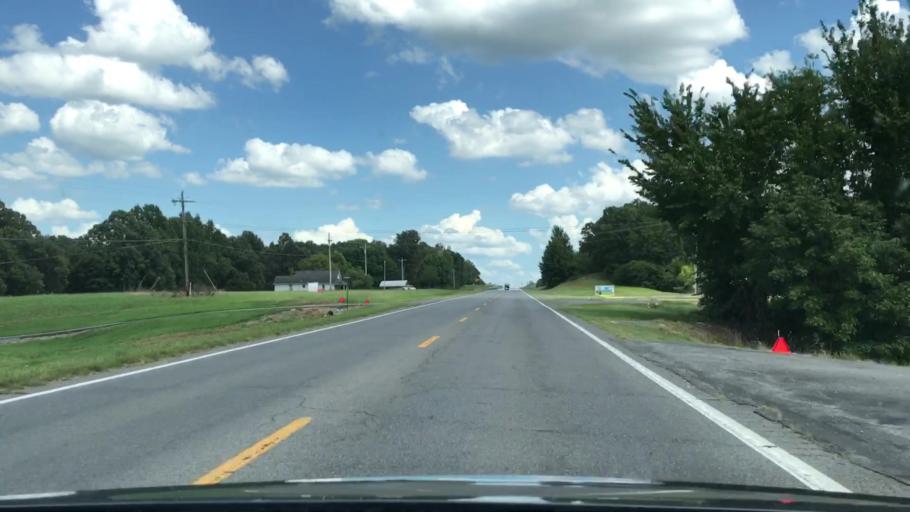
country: US
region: Kentucky
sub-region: Marshall County
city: Calvert City
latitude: 37.0053
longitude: -88.4068
